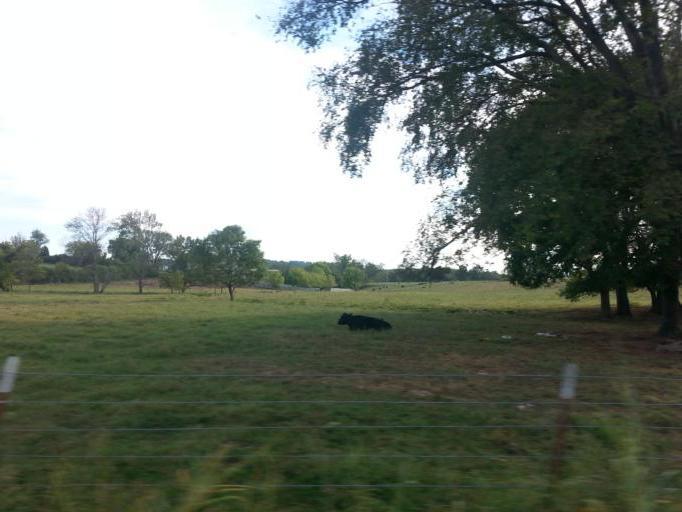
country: US
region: Tennessee
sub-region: Blount County
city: Wildwood
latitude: 35.8208
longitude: -83.9029
